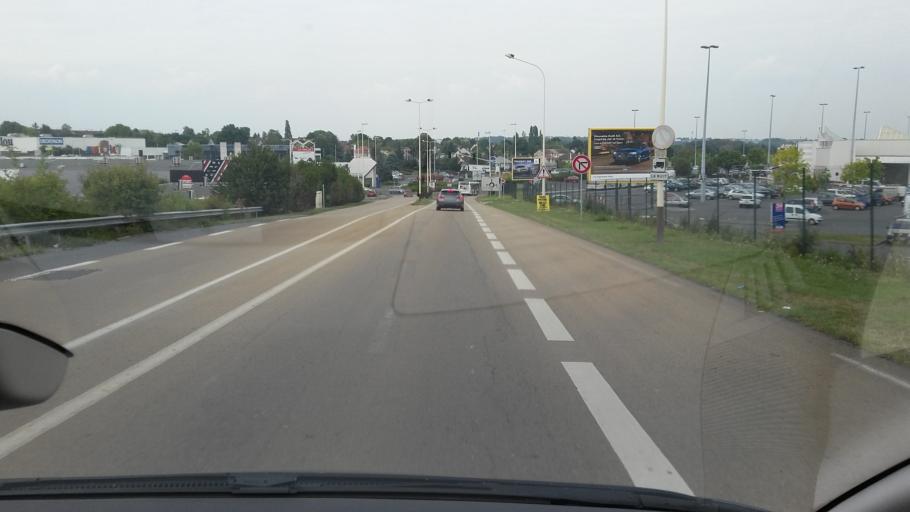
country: FR
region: Champagne-Ardenne
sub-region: Departement de la Marne
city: Cormontreuil
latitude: 49.2131
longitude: 4.0510
